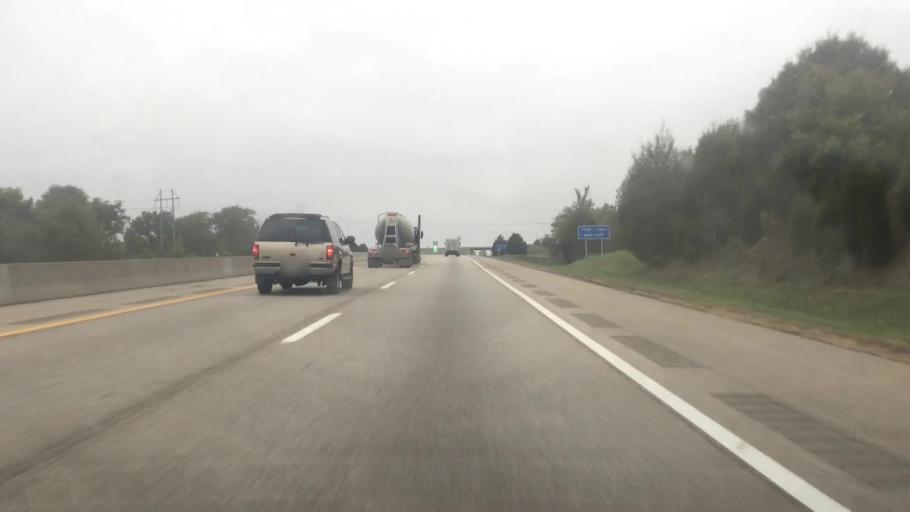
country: US
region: Kansas
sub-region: Douglas County
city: Eudora
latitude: 39.0267
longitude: -95.1246
